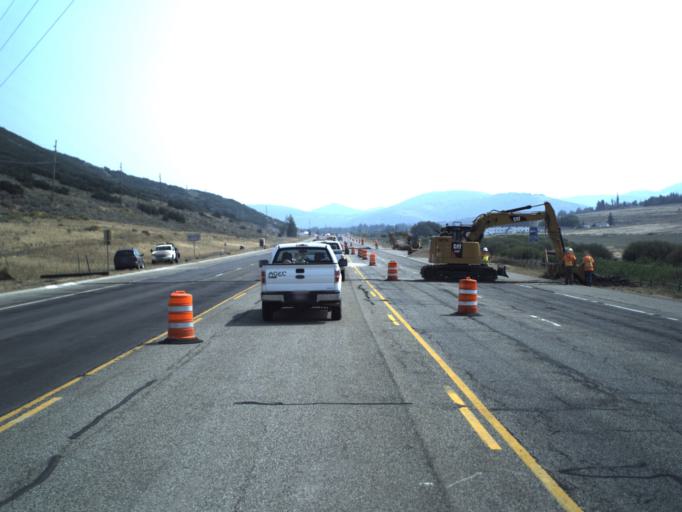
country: US
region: Utah
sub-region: Summit County
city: Snyderville
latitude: 40.6819
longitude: -111.5338
